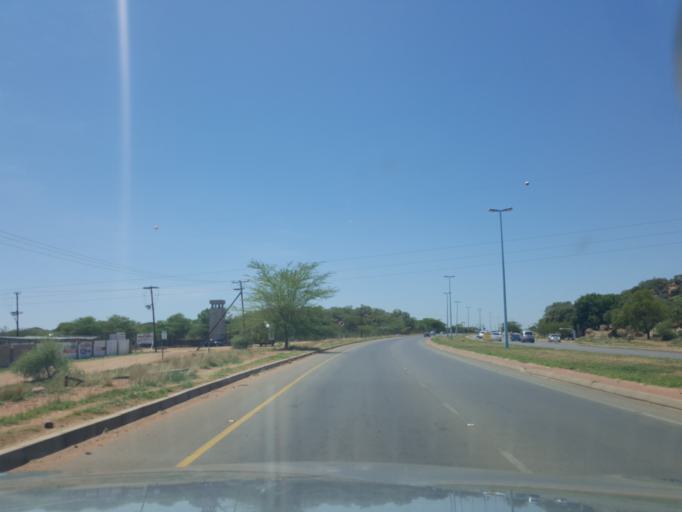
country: BW
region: Kweneng
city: Gaphatshwe
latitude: -24.5969
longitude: 25.8525
